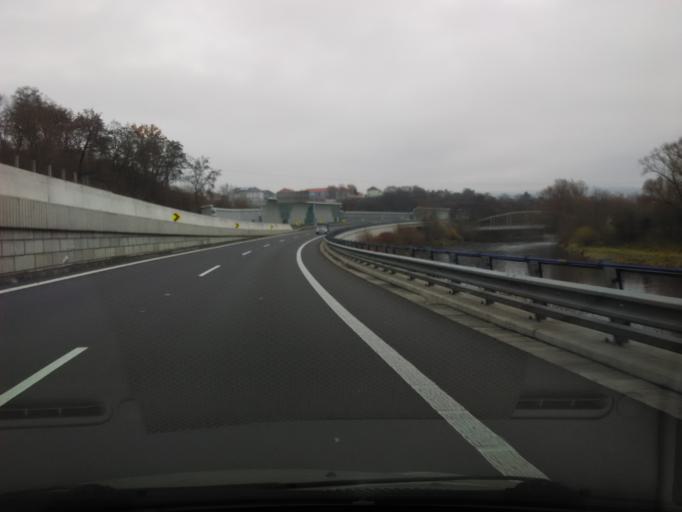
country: SK
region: Banskobystricky
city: Ziar nad Hronom
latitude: 48.5820
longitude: 18.8468
